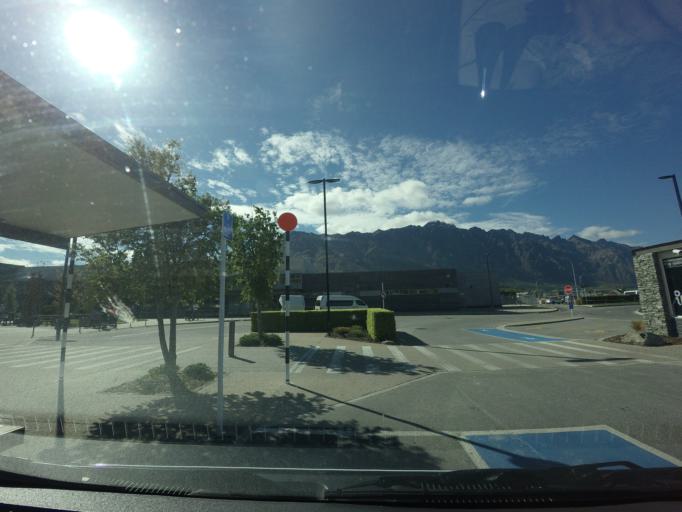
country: NZ
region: Otago
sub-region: Queenstown-Lakes District
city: Queenstown
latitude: -45.0222
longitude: 168.7390
